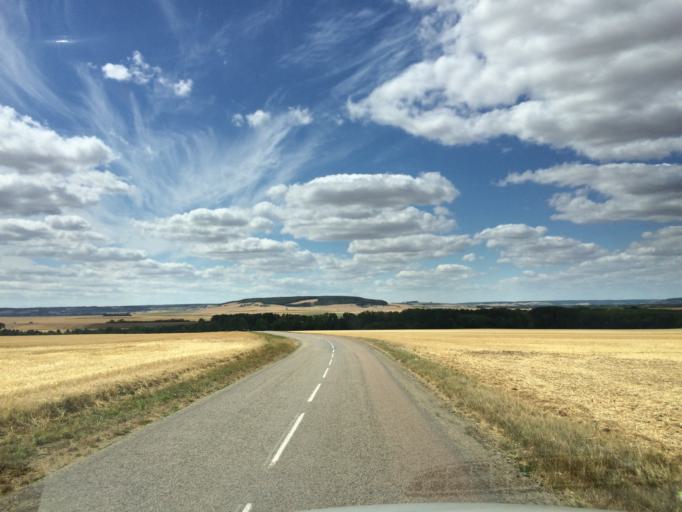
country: FR
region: Bourgogne
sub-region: Departement de l'Yonne
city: Laroche-Saint-Cydroine
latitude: 47.9303
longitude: 3.4524
